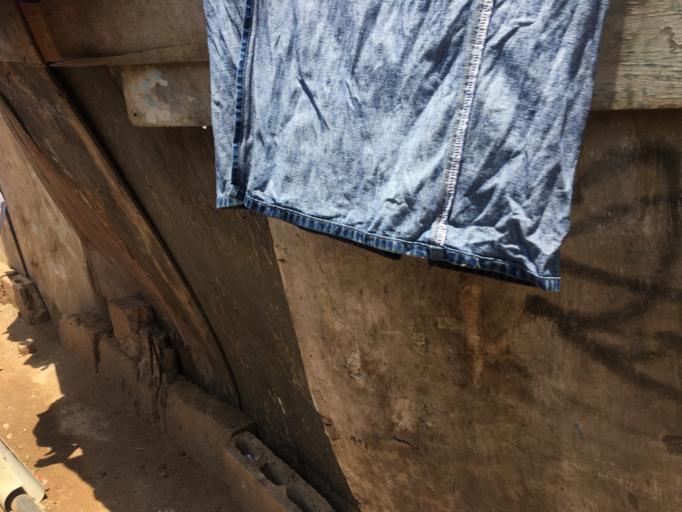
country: GH
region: Greater Accra
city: Accra
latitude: 5.5861
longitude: -0.1932
